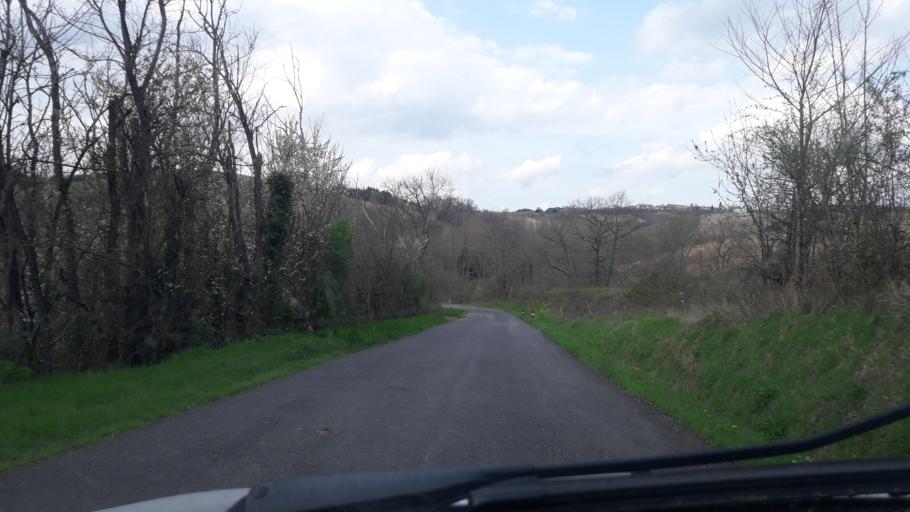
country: FR
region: Midi-Pyrenees
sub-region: Departement de la Haute-Garonne
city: Montesquieu-Volvestre
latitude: 43.2294
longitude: 1.2857
